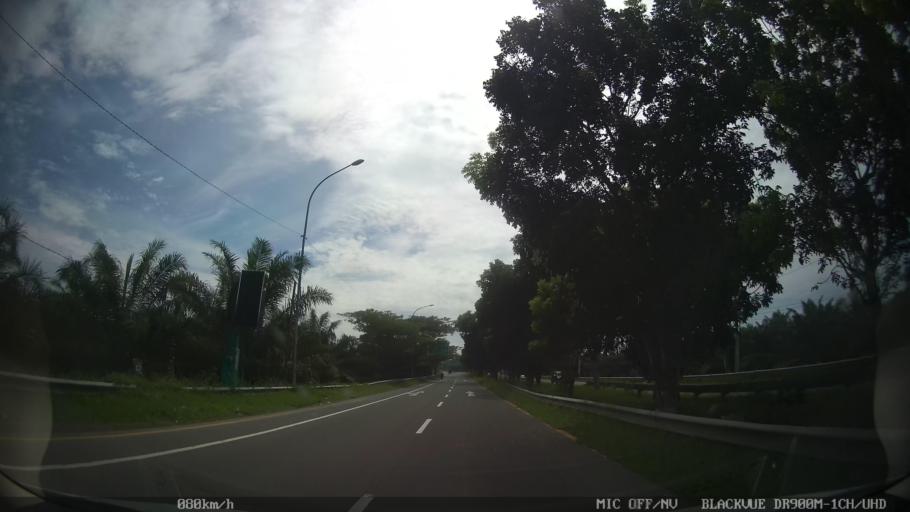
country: ID
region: North Sumatra
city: Percut
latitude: 3.5989
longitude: 98.8363
